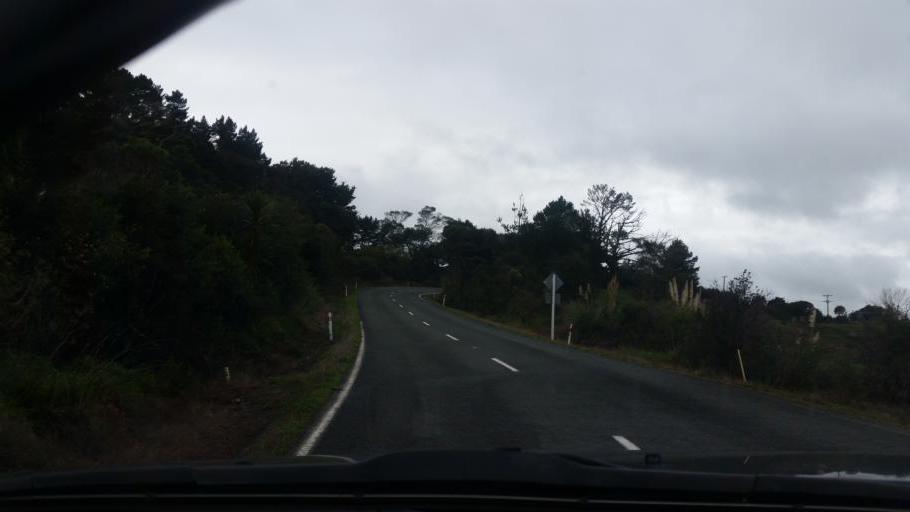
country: NZ
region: Northland
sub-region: Kaipara District
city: Dargaville
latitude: -36.0110
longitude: 173.9424
